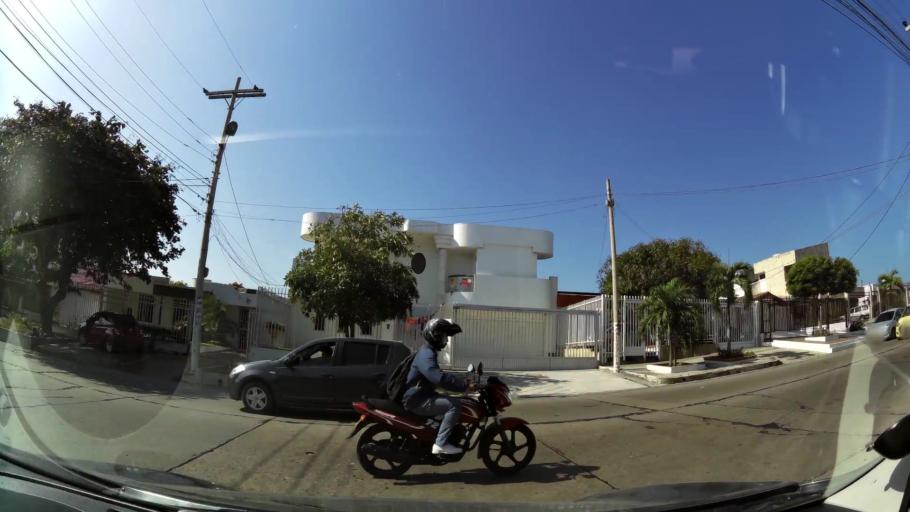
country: CO
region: Atlantico
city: Barranquilla
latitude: 10.9897
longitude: -74.8245
